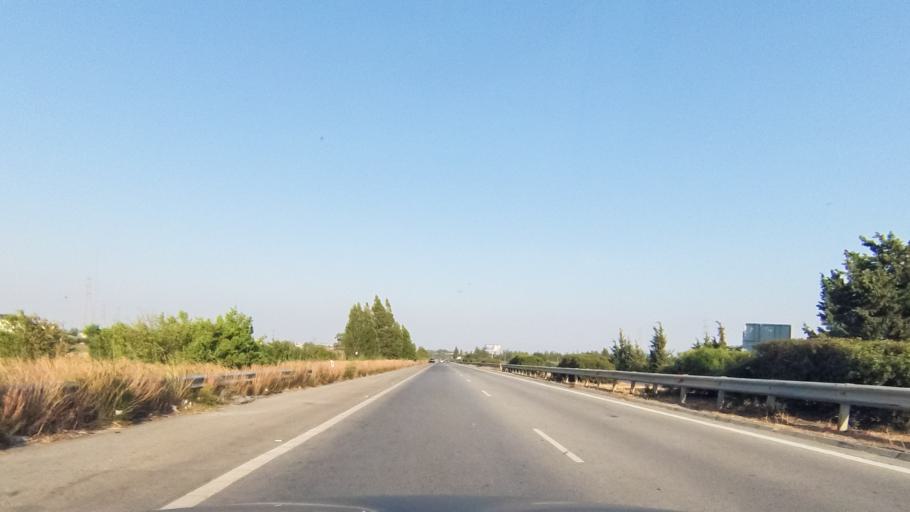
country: CY
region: Limassol
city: Ypsonas
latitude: 34.6915
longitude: 32.9774
